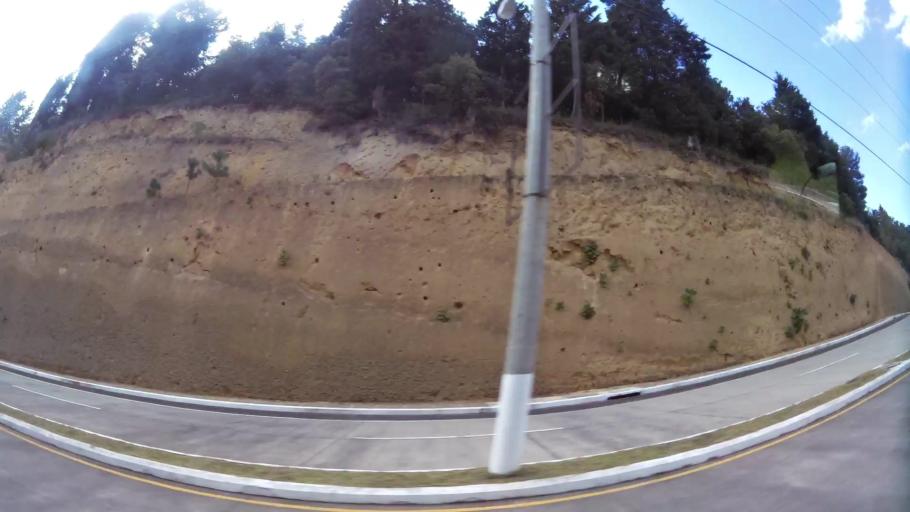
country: GT
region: Quetzaltenango
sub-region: Municipio de La Esperanza
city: La Esperanza
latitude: 14.8357
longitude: -91.5538
